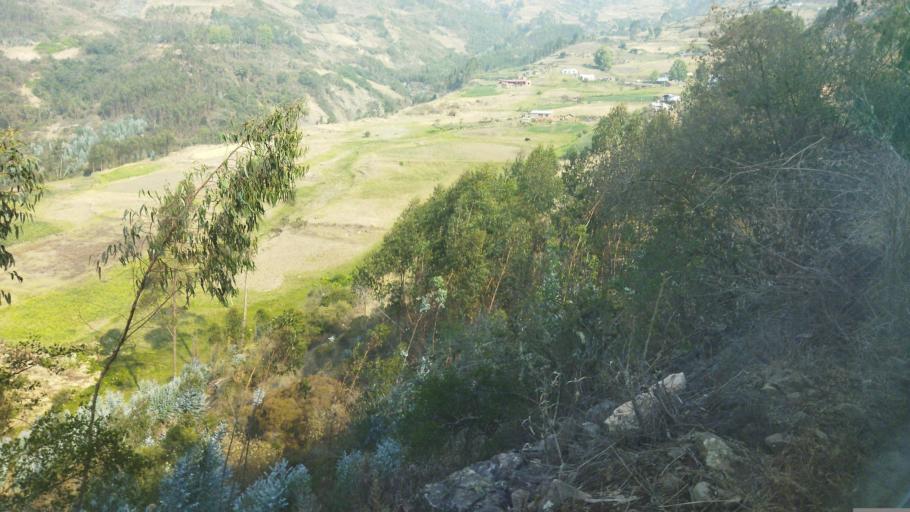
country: BO
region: La Paz
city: Quime
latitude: -16.9820
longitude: -67.1949
